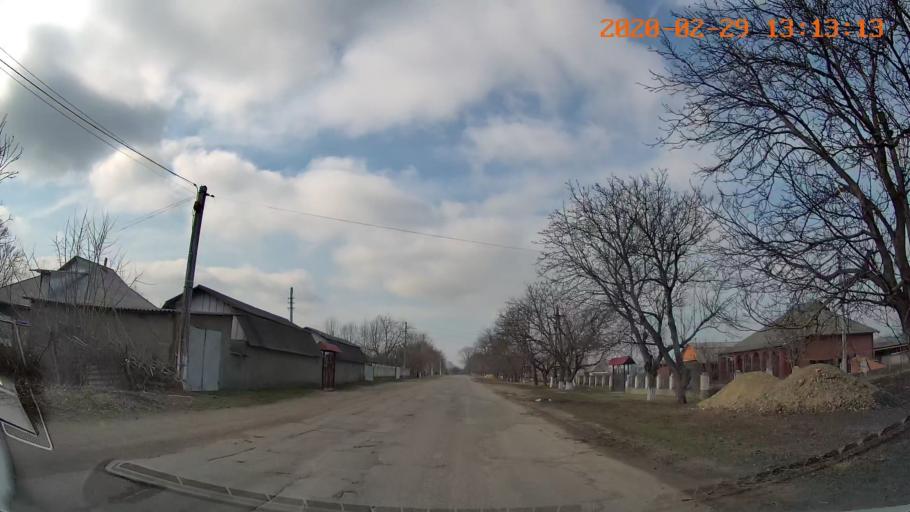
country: MD
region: Telenesti
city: Camenca
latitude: 48.0139
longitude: 28.6868
